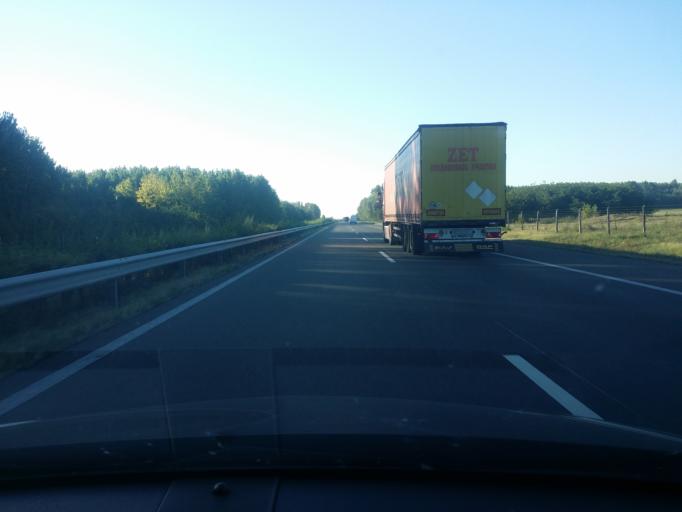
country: HU
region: Csongrad
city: Kistelek
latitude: 46.4957
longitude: 19.9151
